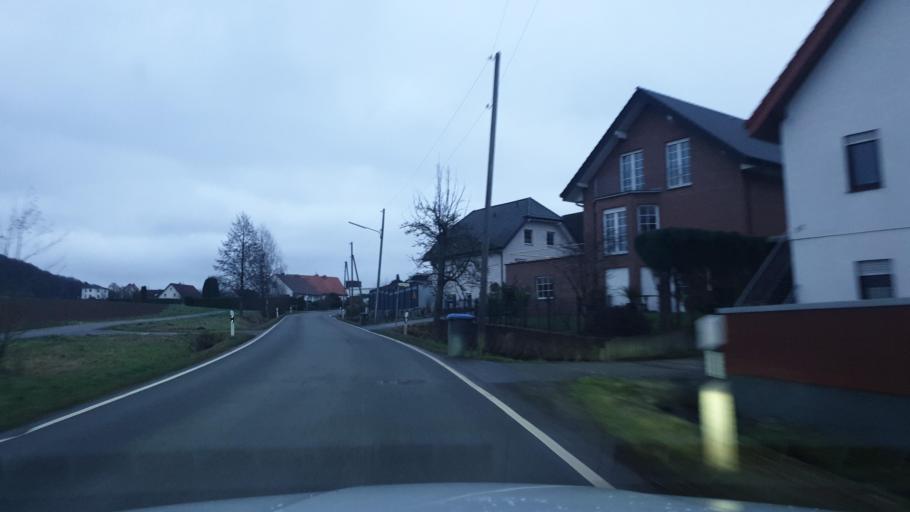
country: DE
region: North Rhine-Westphalia
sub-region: Regierungsbezirk Detmold
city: Vlotho
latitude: 52.1642
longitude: 8.8267
